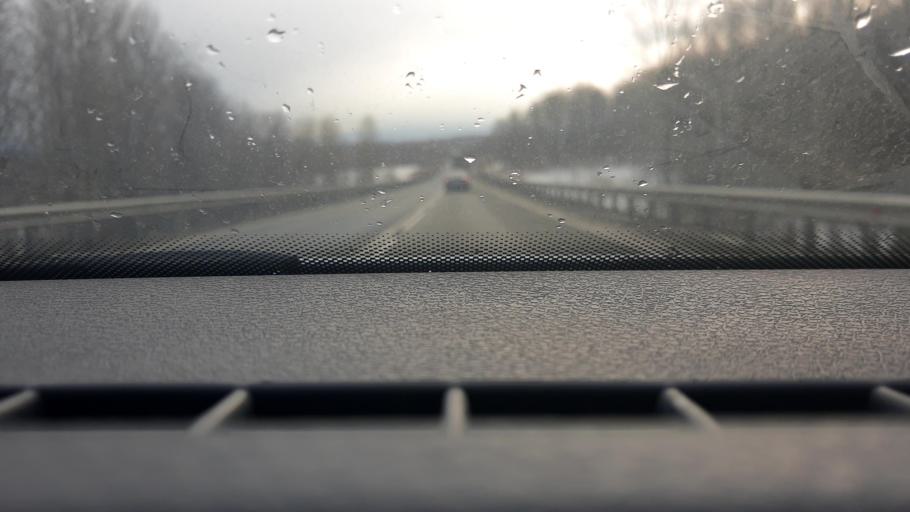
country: RU
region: Bashkortostan
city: Ulu-Telyak
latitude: 54.8433
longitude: 57.0711
